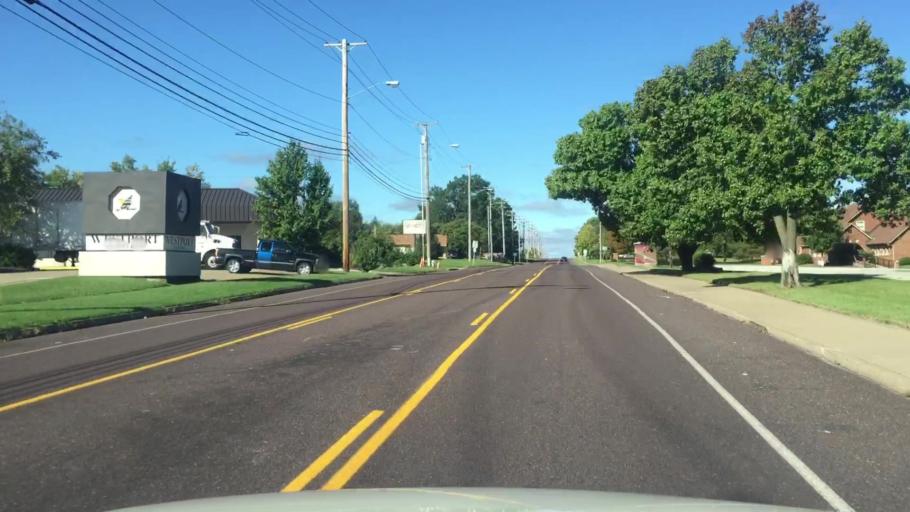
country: US
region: Missouri
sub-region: Boone County
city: Columbia
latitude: 38.9669
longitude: -92.3551
